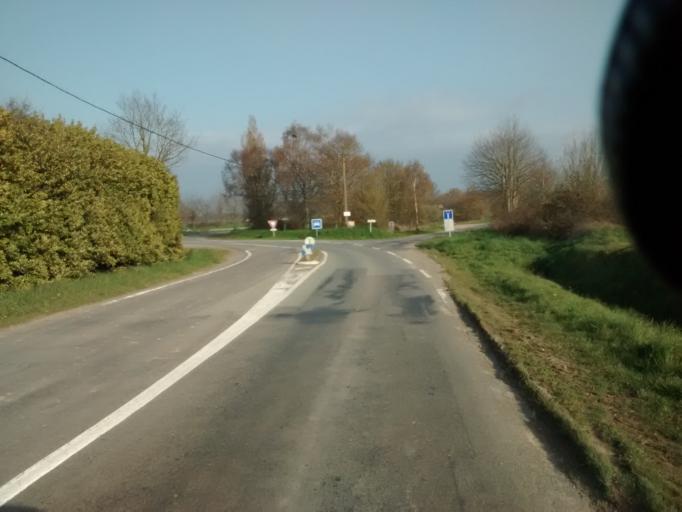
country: FR
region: Brittany
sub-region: Departement d'Ille-et-Vilaine
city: Montauban-de-Bretagne
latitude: 48.1931
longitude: -2.0254
